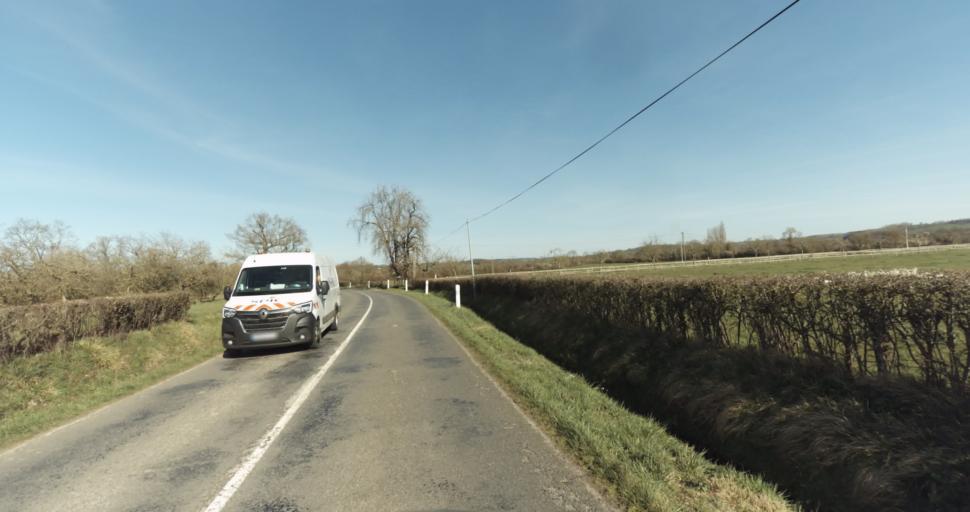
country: FR
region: Lower Normandy
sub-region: Departement du Calvados
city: Saint-Pierre-sur-Dives
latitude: 49.0545
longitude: 0.0519
